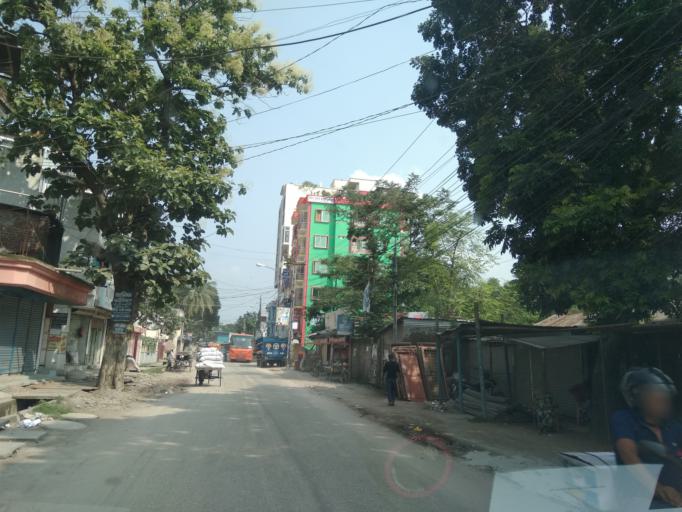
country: BD
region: Rangpur Division
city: Rangpur
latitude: 25.7601
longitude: 89.2321
